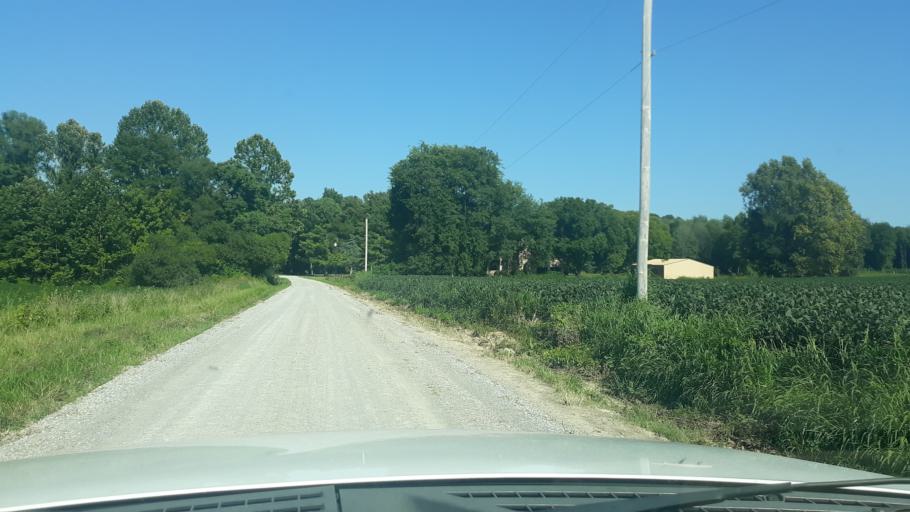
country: US
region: Illinois
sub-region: Saline County
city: Eldorado
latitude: 37.8463
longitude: -88.4932
